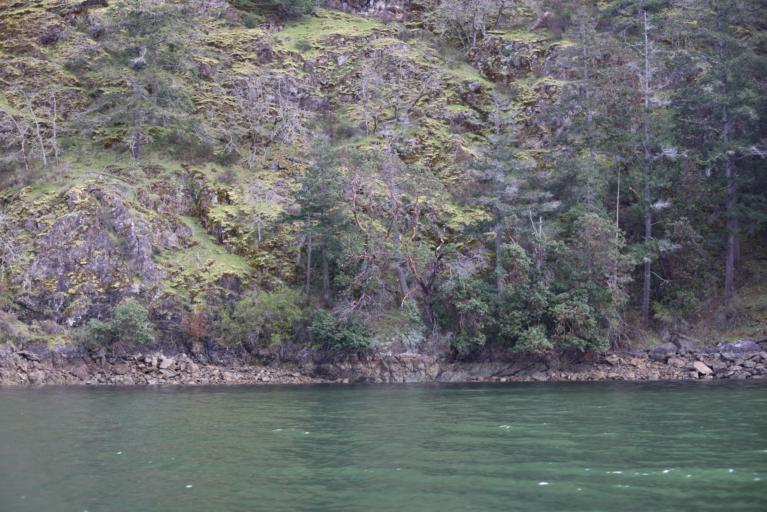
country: CA
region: British Columbia
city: Langford
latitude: 48.5252
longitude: -123.5355
